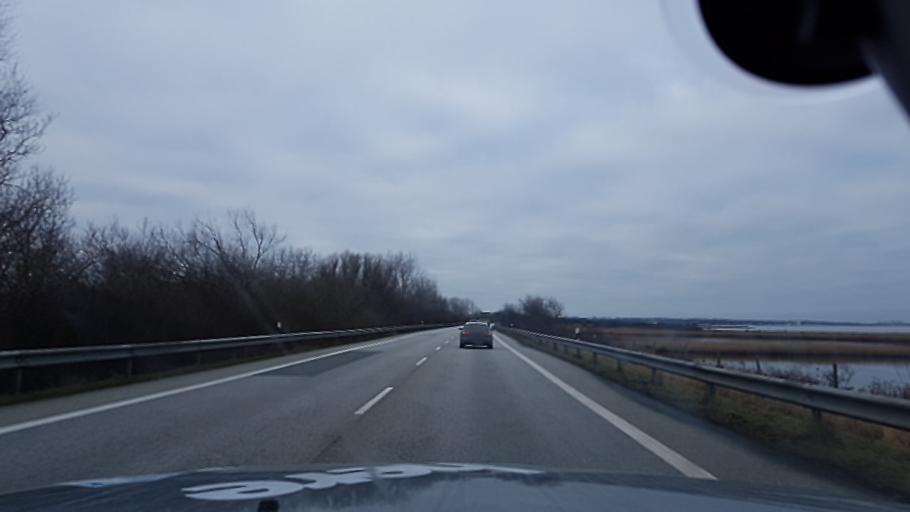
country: DE
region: Schleswig-Holstein
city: Grossenbrode
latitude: 54.3771
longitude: 11.0809
